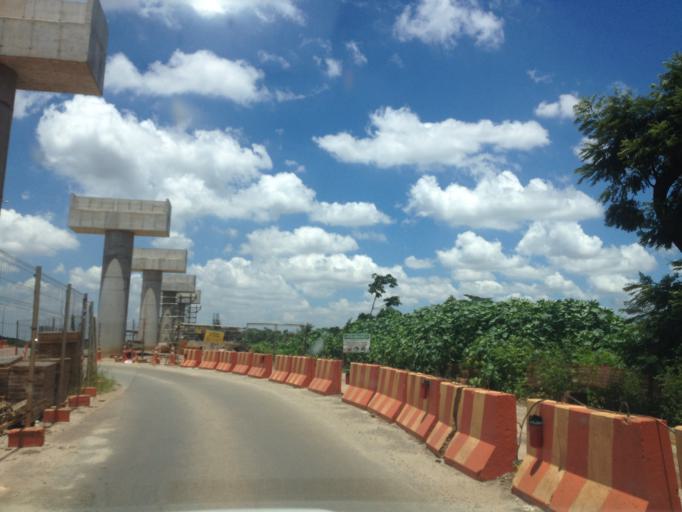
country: BR
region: Sao Paulo
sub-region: Guarulhos
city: Guarulhos
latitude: -23.4308
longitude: -46.4935
